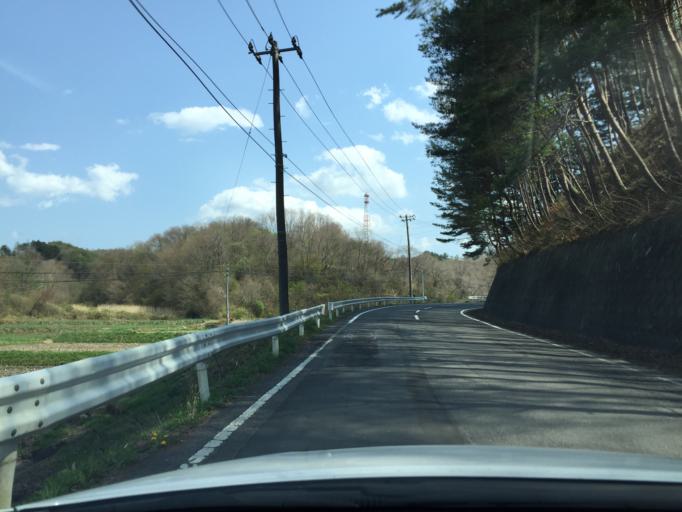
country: JP
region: Fukushima
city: Namie
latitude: 37.3890
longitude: 140.7982
